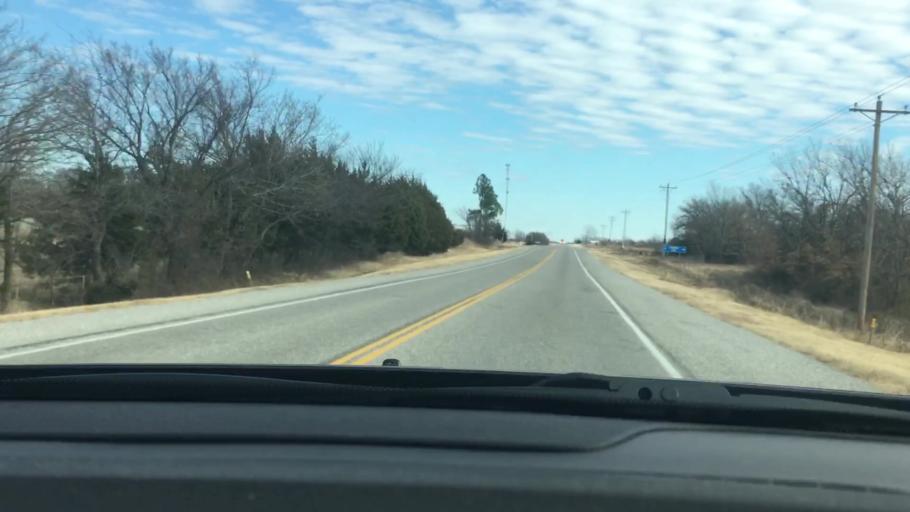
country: US
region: Oklahoma
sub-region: Garvin County
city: Stratford
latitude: 34.7965
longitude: -97.0576
